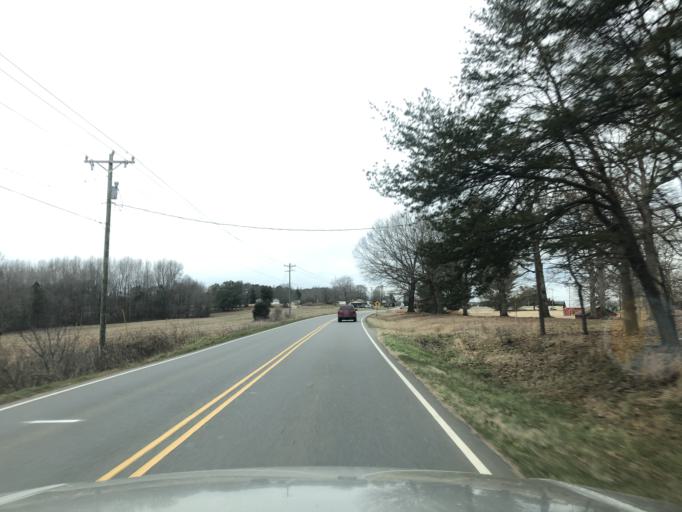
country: US
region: North Carolina
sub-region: Cleveland County
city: Shelby
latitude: 35.3341
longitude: -81.5009
